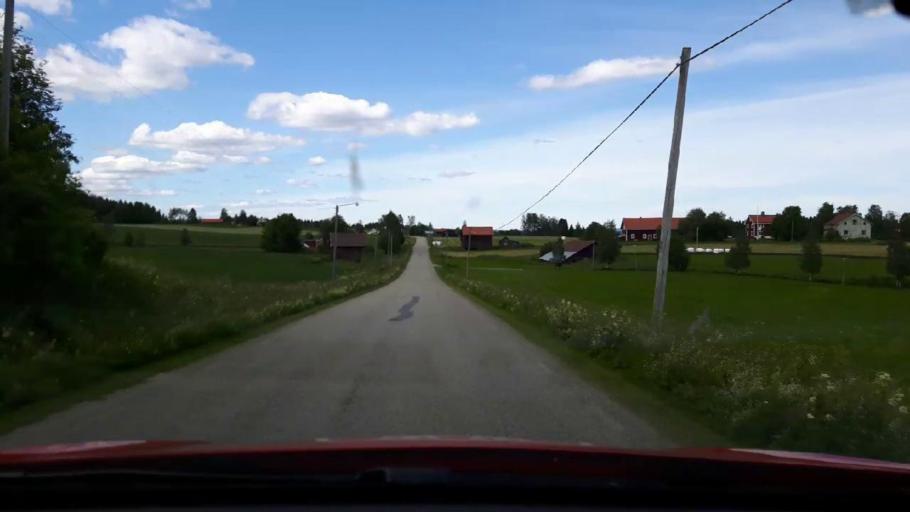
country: SE
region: Jaemtland
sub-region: Bergs Kommun
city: Hoverberg
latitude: 62.8278
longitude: 14.4593
